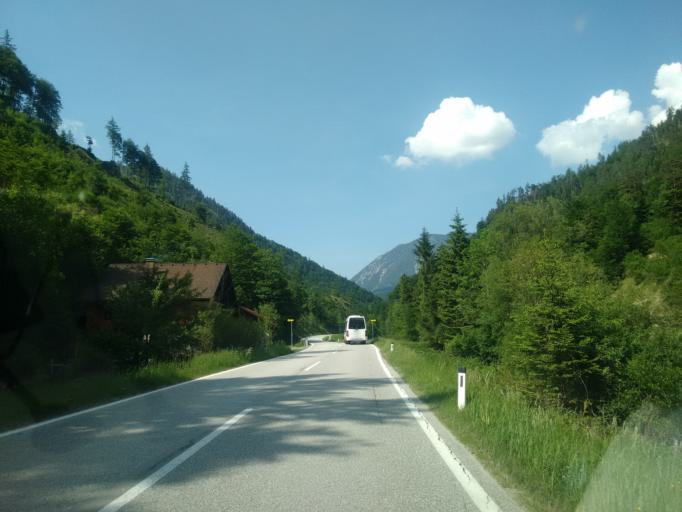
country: AT
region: Upper Austria
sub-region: Politischer Bezirk Kirchdorf an der Krems
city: Rossleithen
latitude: 47.7528
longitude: 14.1627
